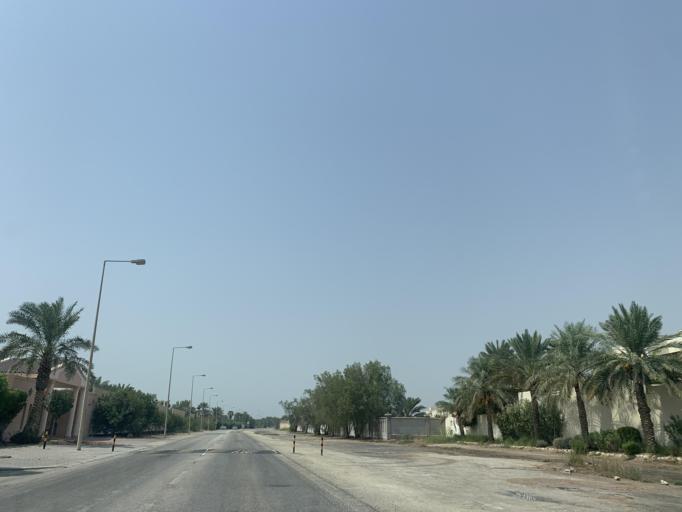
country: BH
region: Central Governorate
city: Madinat Hamad
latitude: 26.1612
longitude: 50.4660
